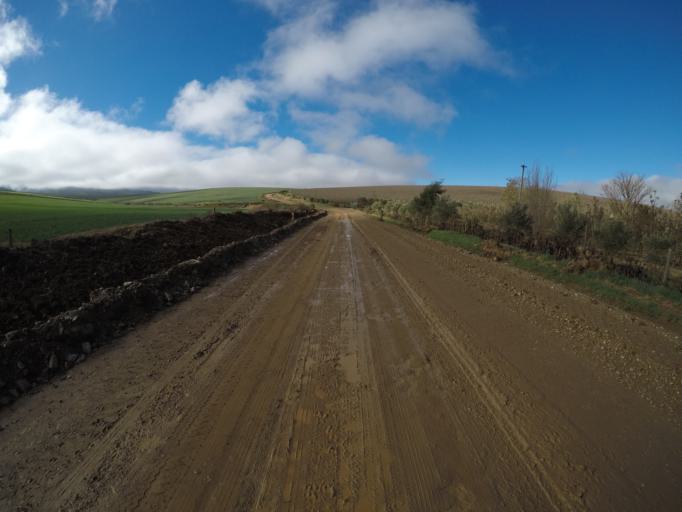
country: ZA
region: Western Cape
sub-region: Overberg District Municipality
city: Caledon
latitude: -34.1099
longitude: 19.7523
